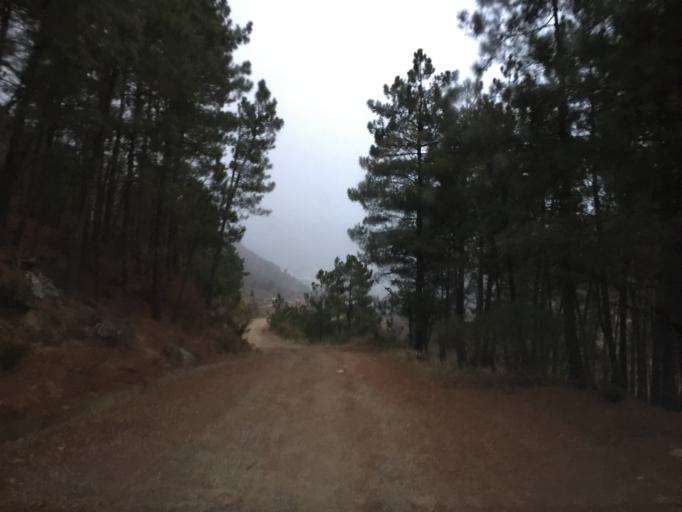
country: PT
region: Guarda
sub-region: Manteigas
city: Manteigas
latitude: 40.3718
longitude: -7.5516
